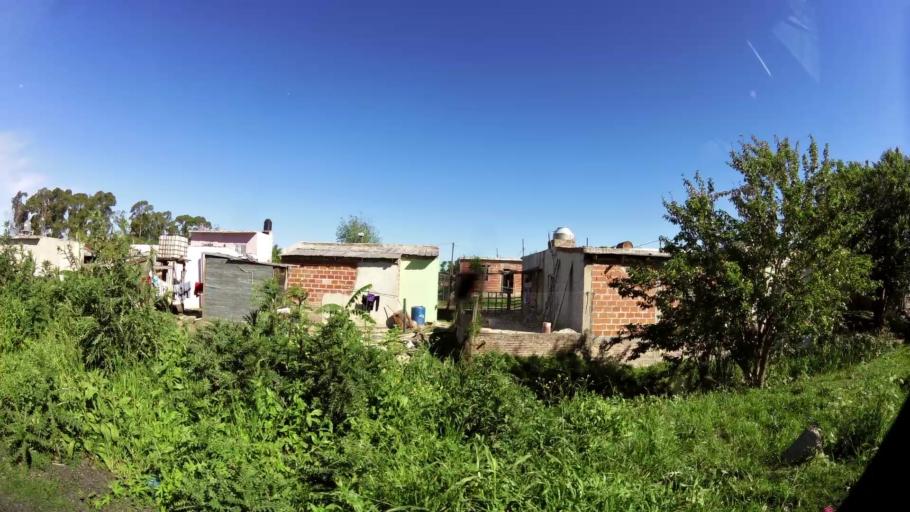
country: AR
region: Buenos Aires
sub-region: Partido de Quilmes
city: Quilmes
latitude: -34.7587
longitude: -58.3103
